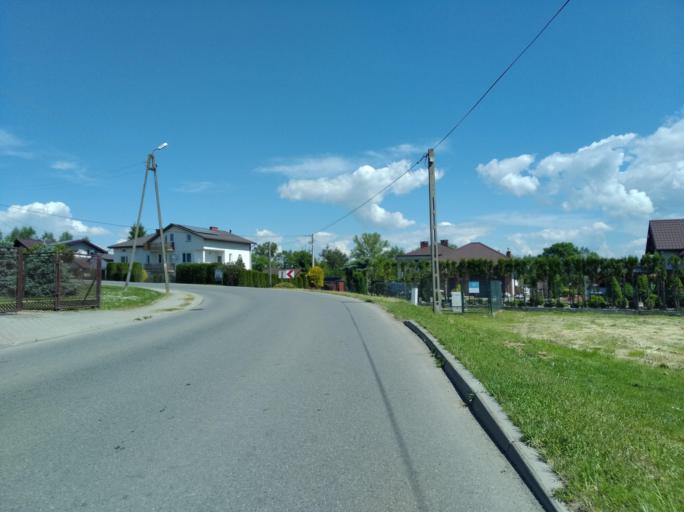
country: PL
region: Subcarpathian Voivodeship
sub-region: Powiat krosnienski
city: Jedlicze
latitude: 49.7079
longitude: 21.6249
